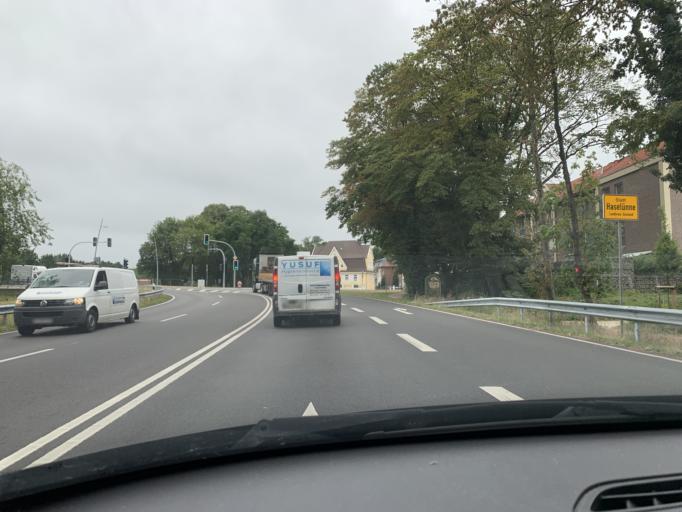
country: DE
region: Lower Saxony
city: Haselunne
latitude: 52.6719
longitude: 7.4883
